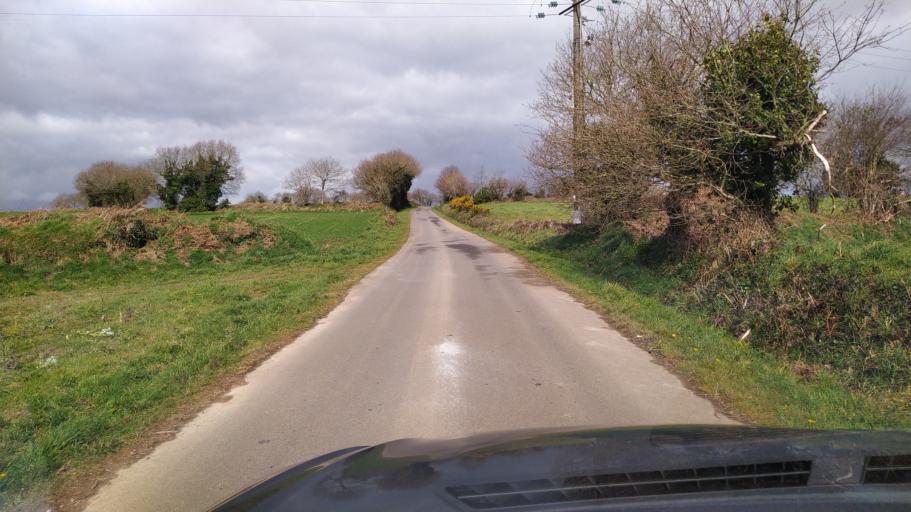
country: FR
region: Brittany
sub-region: Departement du Finistere
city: Bodilis
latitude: 48.5208
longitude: -4.1193
